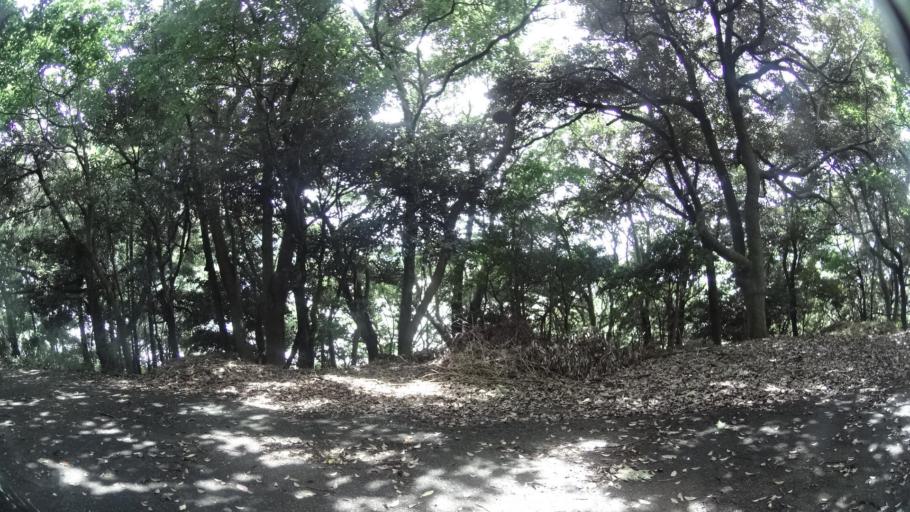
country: JP
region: Kyoto
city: Maizuru
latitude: 35.5302
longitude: 135.3413
